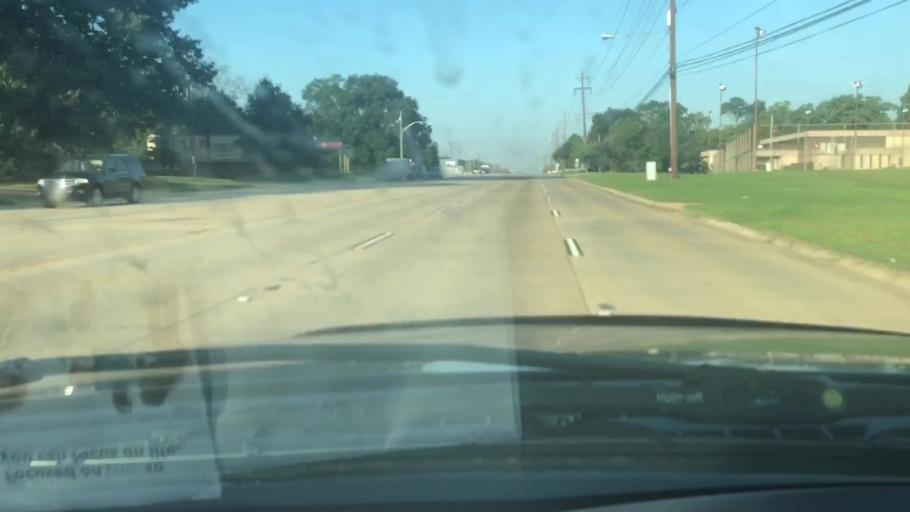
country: US
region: Texas
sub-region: Bowie County
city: Wake Village
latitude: 33.4206
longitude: -94.0828
